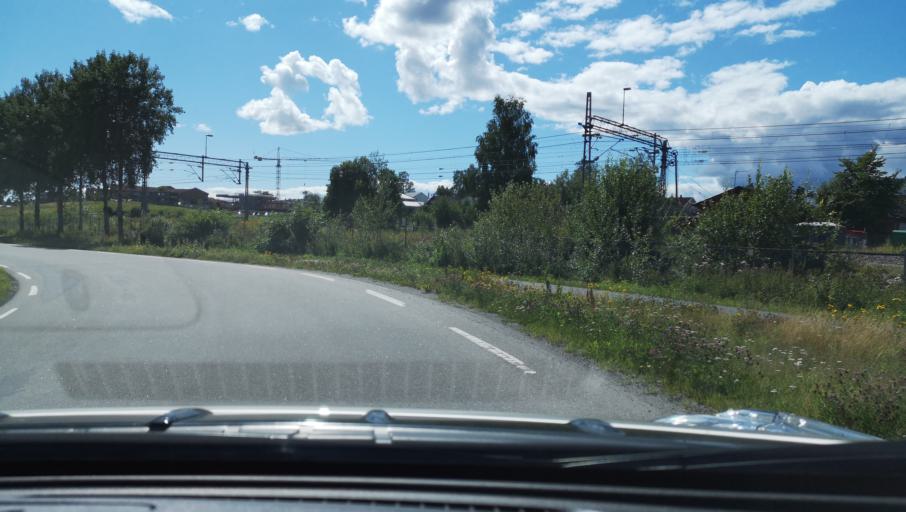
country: NO
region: Akershus
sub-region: As
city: As
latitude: 59.6615
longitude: 10.7964
